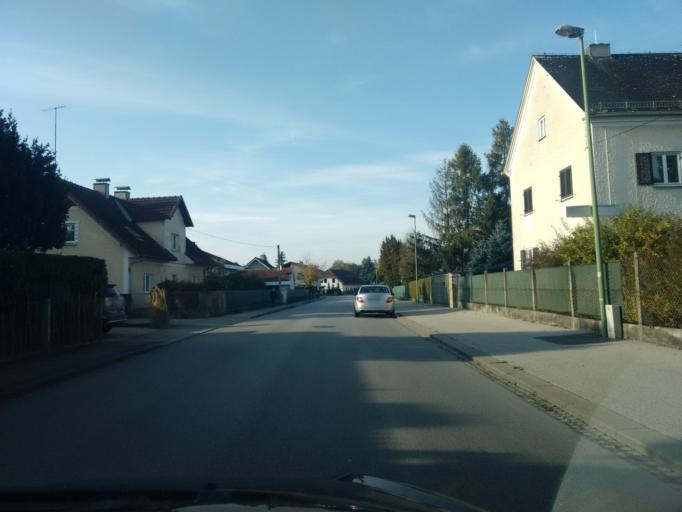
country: AT
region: Upper Austria
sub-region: Wels Stadt
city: Wels
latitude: 48.1718
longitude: 14.0066
